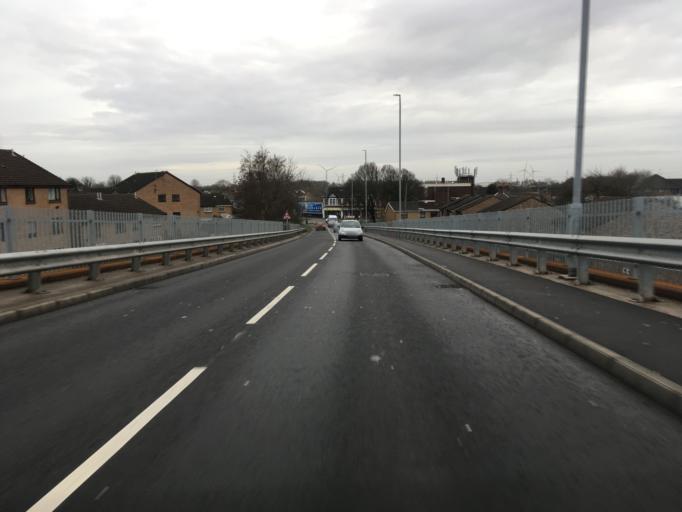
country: GB
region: Wales
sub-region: Newport
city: Caerleon
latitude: 51.5842
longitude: -2.9632
